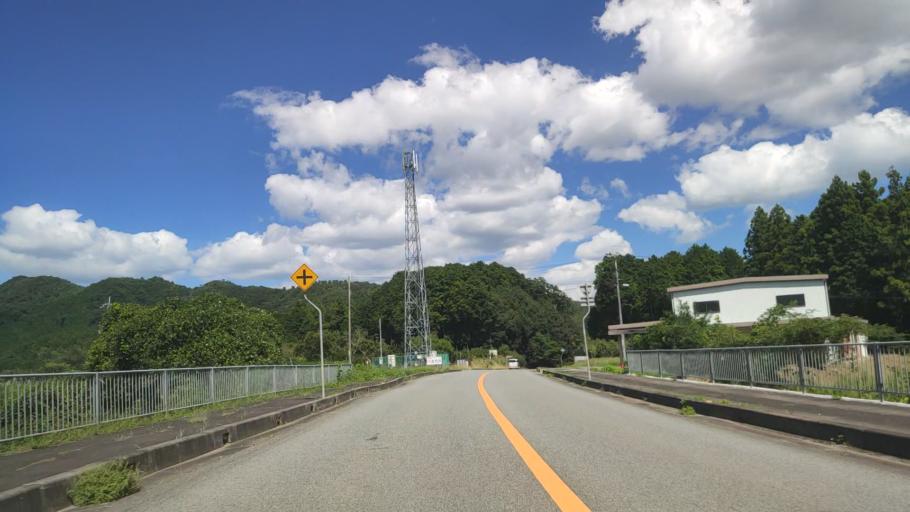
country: JP
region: Kyoto
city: Fukuchiyama
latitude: 35.2421
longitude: 135.1235
